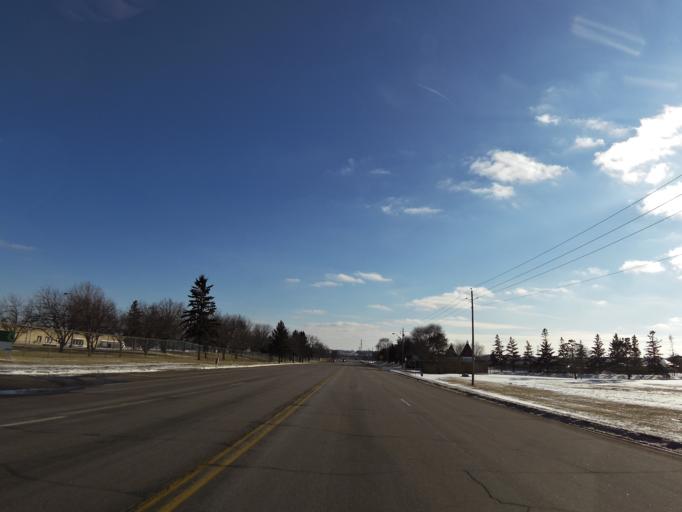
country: US
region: Minnesota
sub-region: Scott County
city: Shakopee
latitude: 44.7911
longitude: -93.4698
